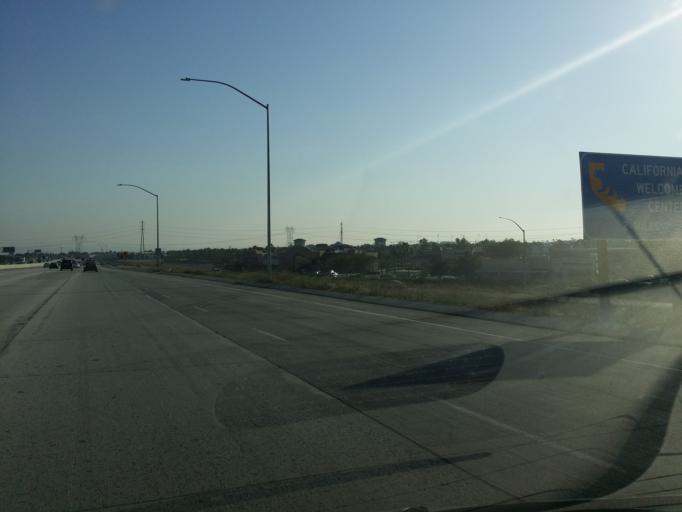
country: US
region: California
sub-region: San Bernardino County
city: Rancho Cucamonga
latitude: 34.1060
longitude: -117.5329
